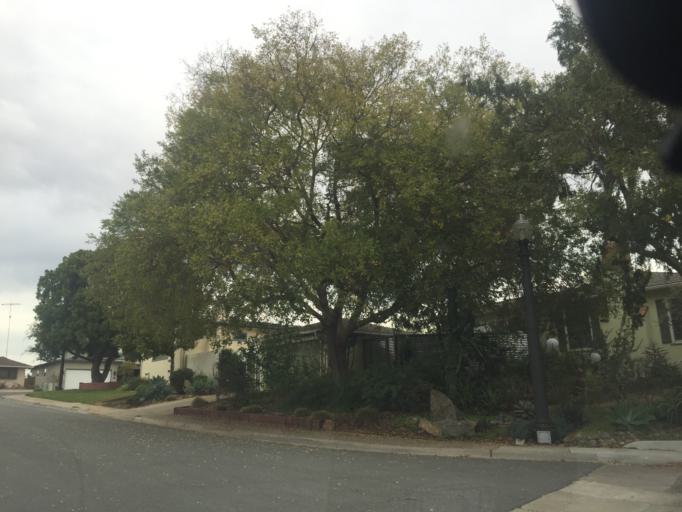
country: US
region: California
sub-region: San Diego County
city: Lemon Grove
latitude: 32.7675
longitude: -117.0919
